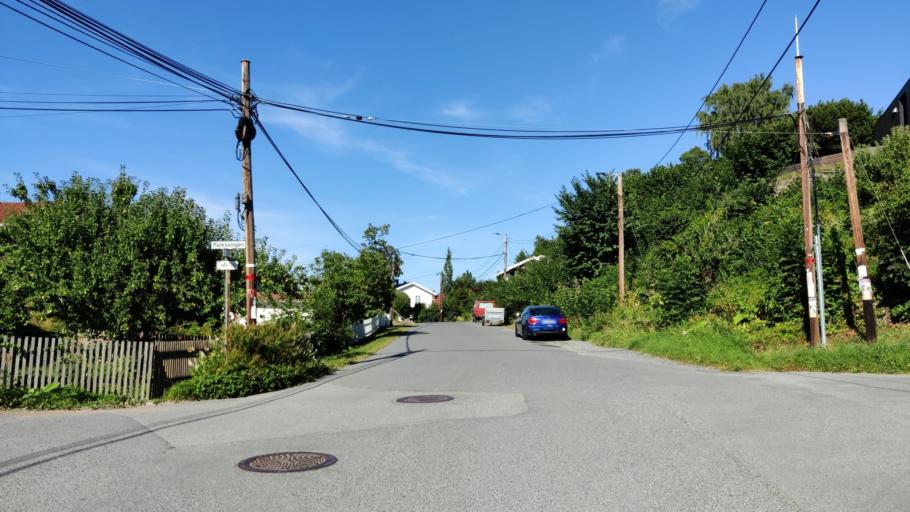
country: NO
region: Akershus
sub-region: Baerum
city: Lysaker
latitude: 59.9258
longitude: 10.5993
